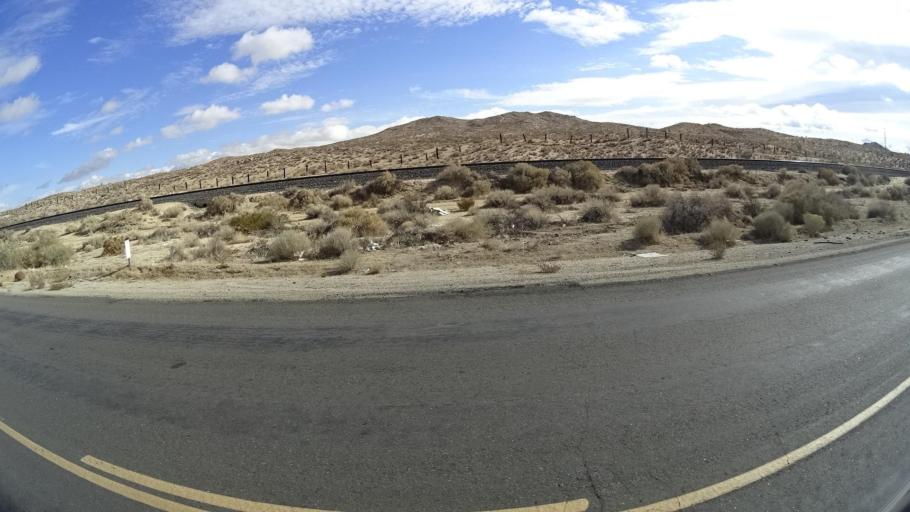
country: US
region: California
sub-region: Kern County
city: Rosamond
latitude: 34.8929
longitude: -118.1629
